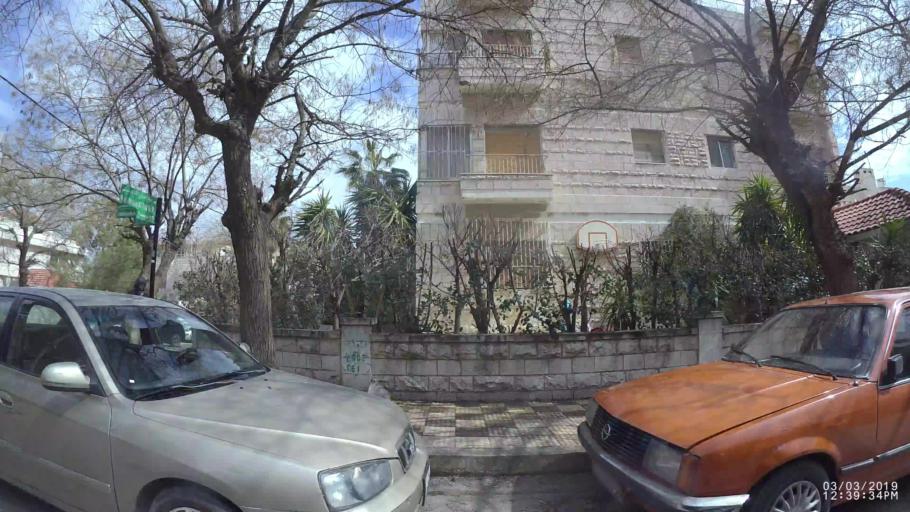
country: JO
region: Amman
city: Amman
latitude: 31.9716
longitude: 35.8995
